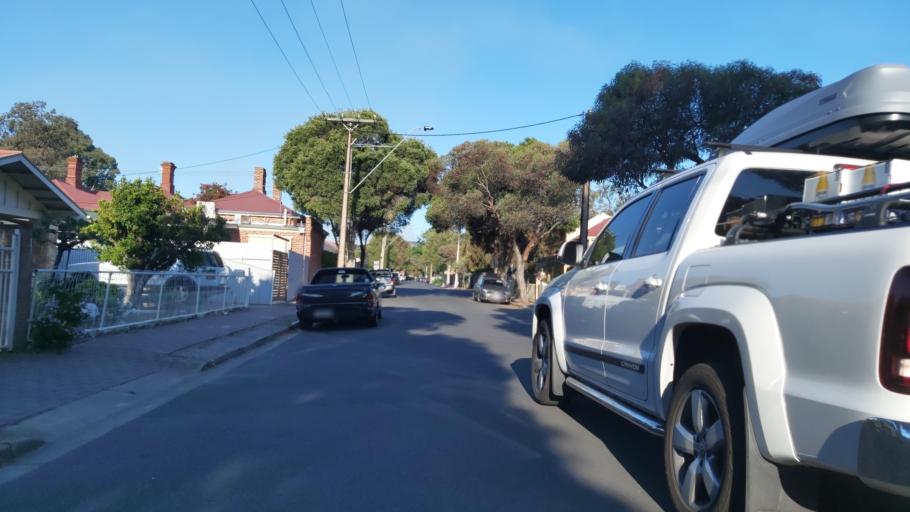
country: AU
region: South Australia
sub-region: Unley
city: Fullarton
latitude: -34.9461
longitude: 138.6180
